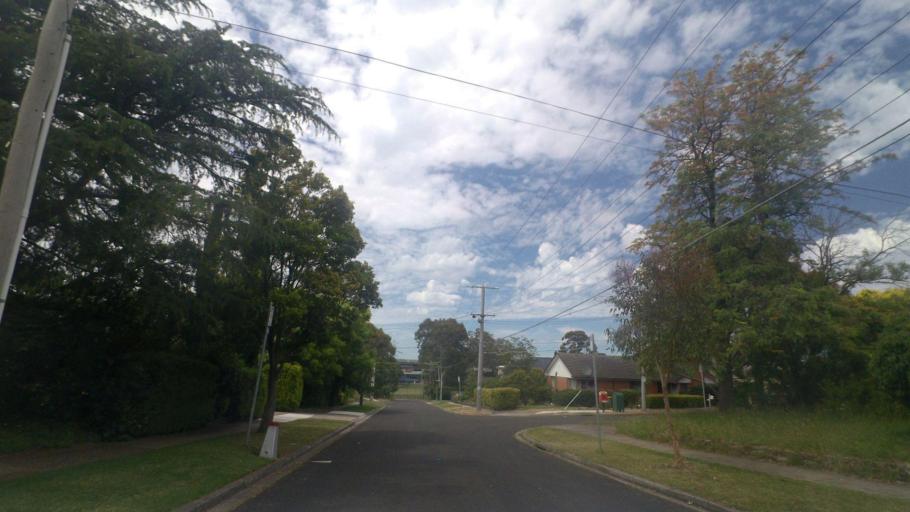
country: AU
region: Victoria
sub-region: Banyule
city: Viewbank
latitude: -37.7396
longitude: 145.0873
